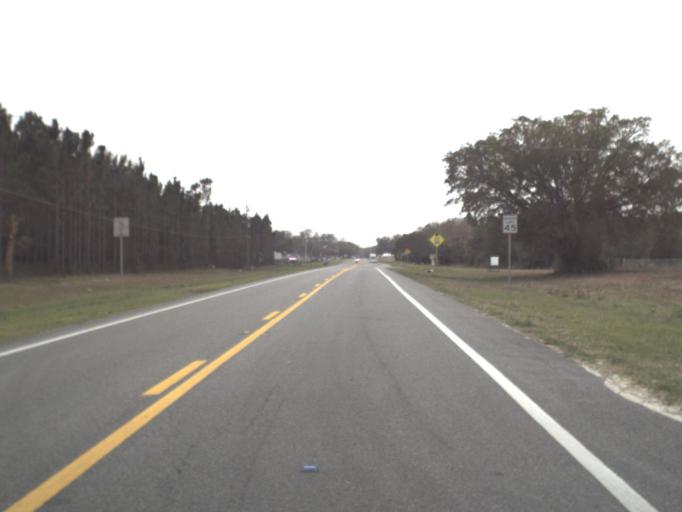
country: US
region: Florida
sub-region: Wakulla County
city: Crawfordville
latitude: 30.1112
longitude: -84.3760
